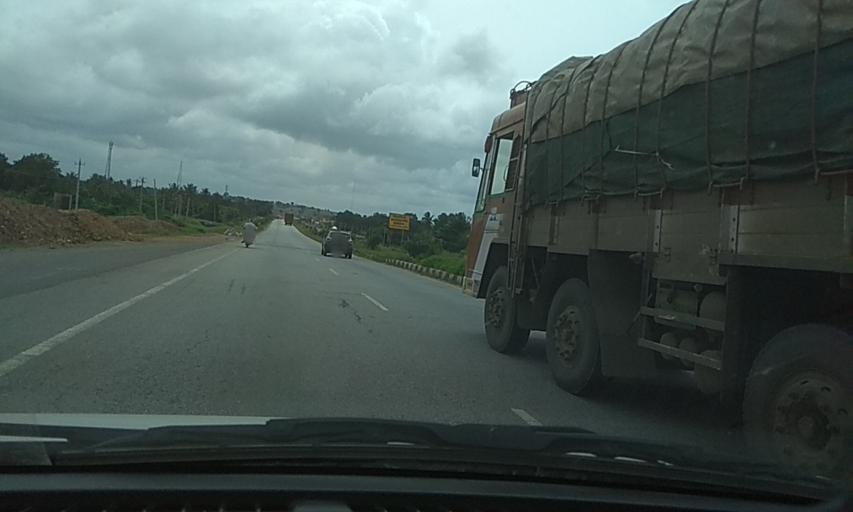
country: IN
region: Karnataka
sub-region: Davanagere
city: Mayakonda
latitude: 14.3667
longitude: 76.1528
